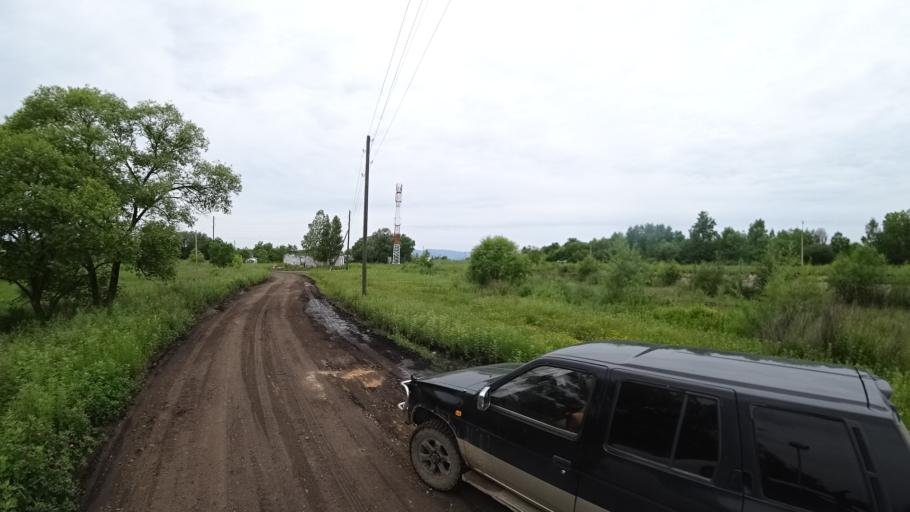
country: RU
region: Primorskiy
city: Novosysoyevka
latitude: 44.2095
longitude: 133.3411
